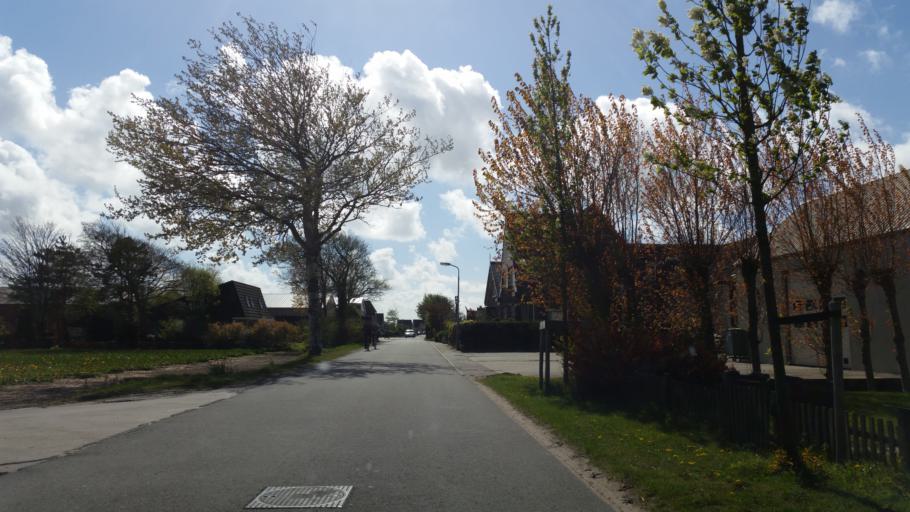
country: NL
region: South Holland
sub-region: Gemeente Noordwijkerhout
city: Noordwijkerhout
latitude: 52.2605
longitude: 4.4756
